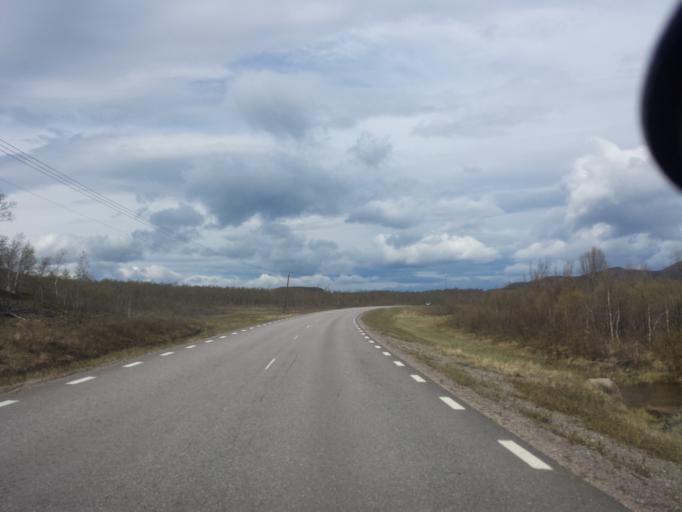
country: SE
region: Norrbotten
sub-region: Kiruna Kommun
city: Kiruna
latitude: 68.1646
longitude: 19.7824
